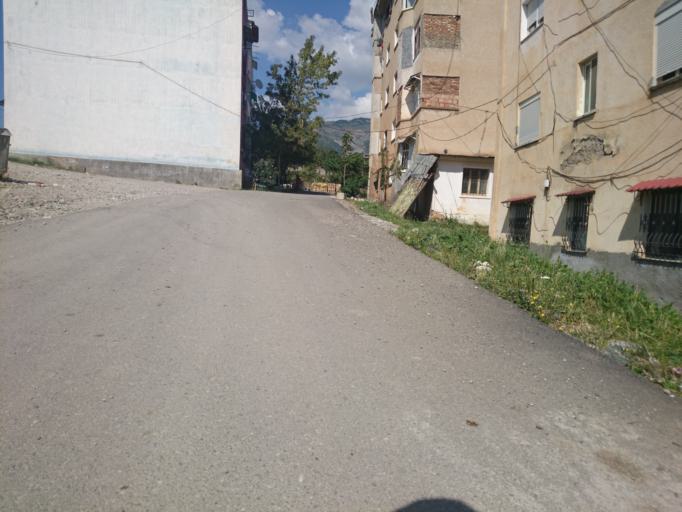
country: AL
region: Diber
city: Peshkopi
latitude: 41.6810
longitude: 20.4244
